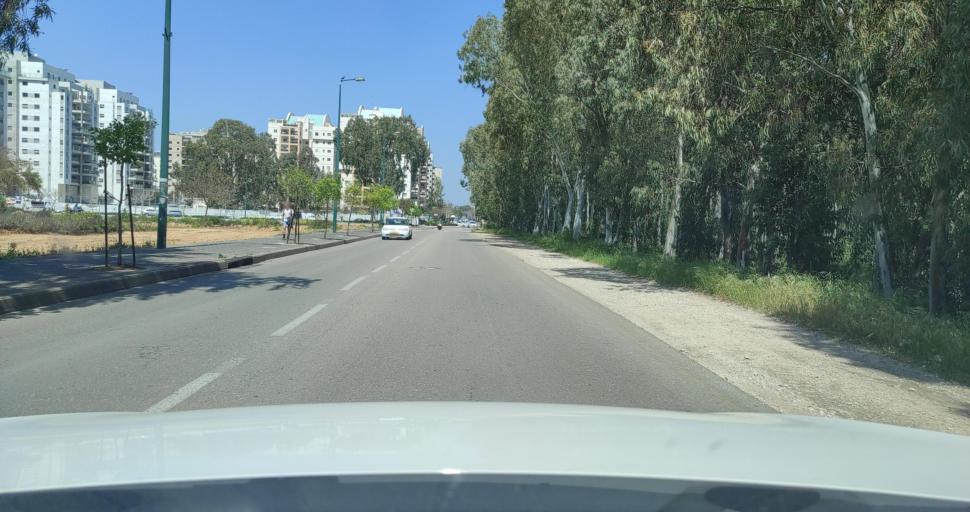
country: IL
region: Central District
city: Nordiyya
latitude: 32.3053
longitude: 34.8742
